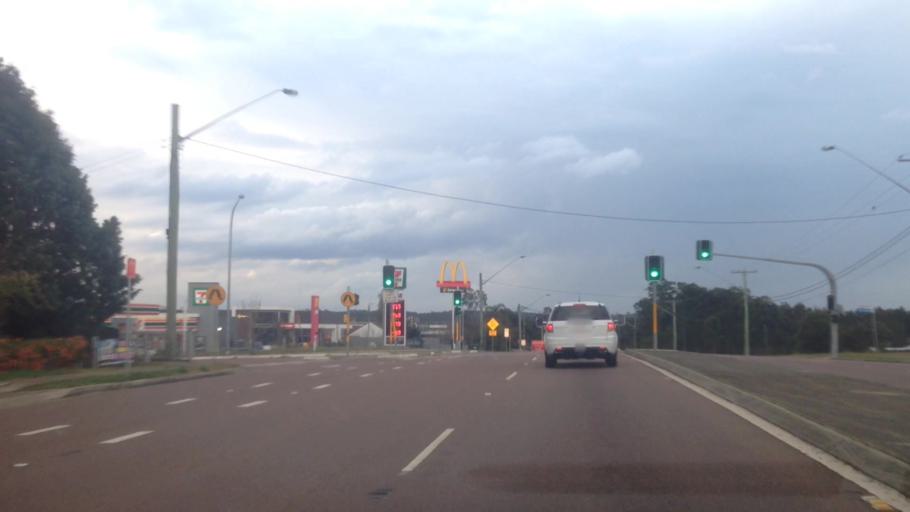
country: AU
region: New South Wales
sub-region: Wyong Shire
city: Tuggerawong
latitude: -33.2659
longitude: 151.4549
